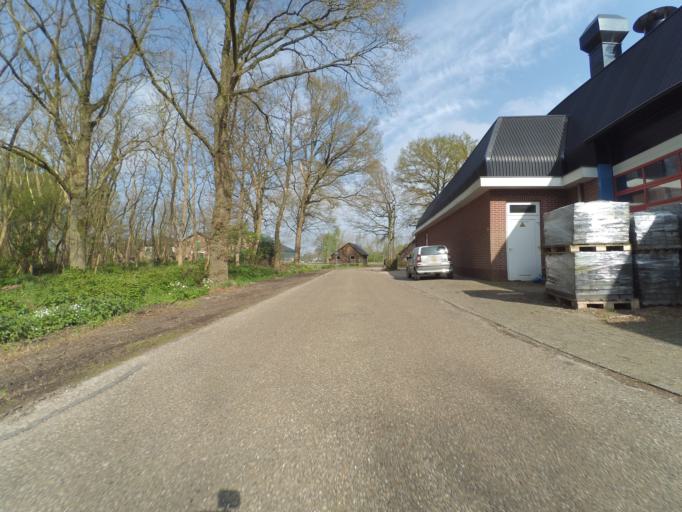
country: NL
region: Gelderland
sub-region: Gemeente Apeldoorn
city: Uddel
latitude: 52.2801
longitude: 5.7738
